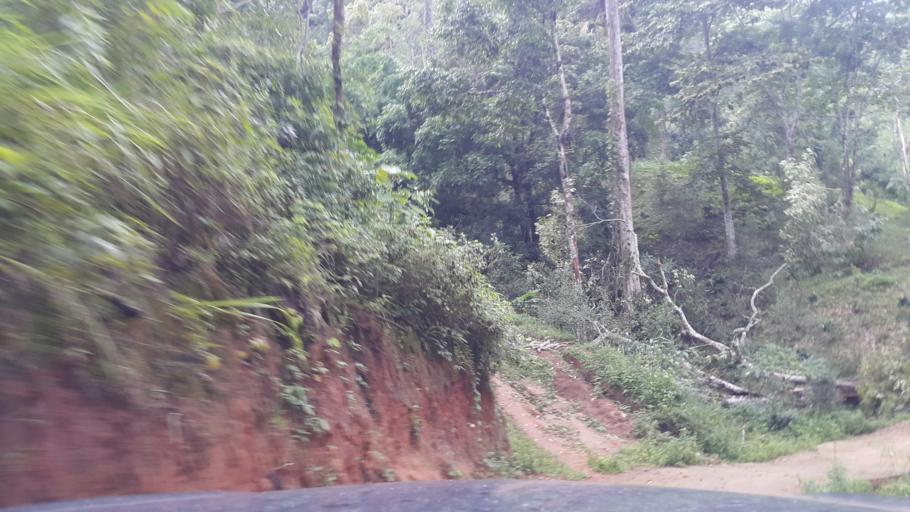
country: TH
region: Lampang
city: Wang Nuea
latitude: 19.1148
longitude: 99.3633
